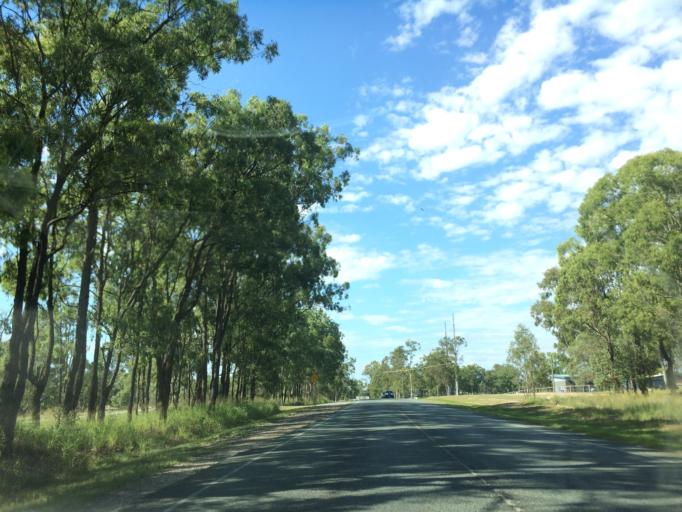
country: AU
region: Queensland
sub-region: Logan
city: Park Ridge South
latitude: -27.7264
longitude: 152.9845
